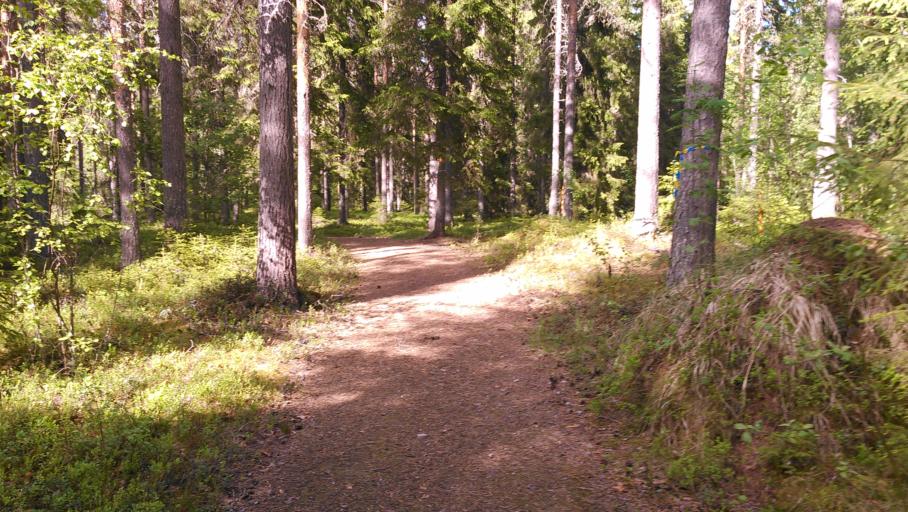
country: SE
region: Vaesterbotten
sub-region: Vannas Kommun
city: Vannasby
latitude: 64.0187
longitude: 19.9030
